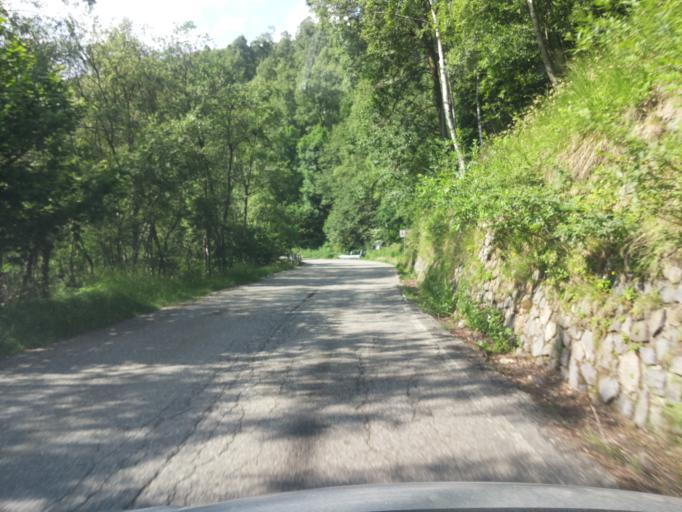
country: IT
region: Piedmont
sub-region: Provincia di Biella
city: Quittengo
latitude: 45.6559
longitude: 8.0364
